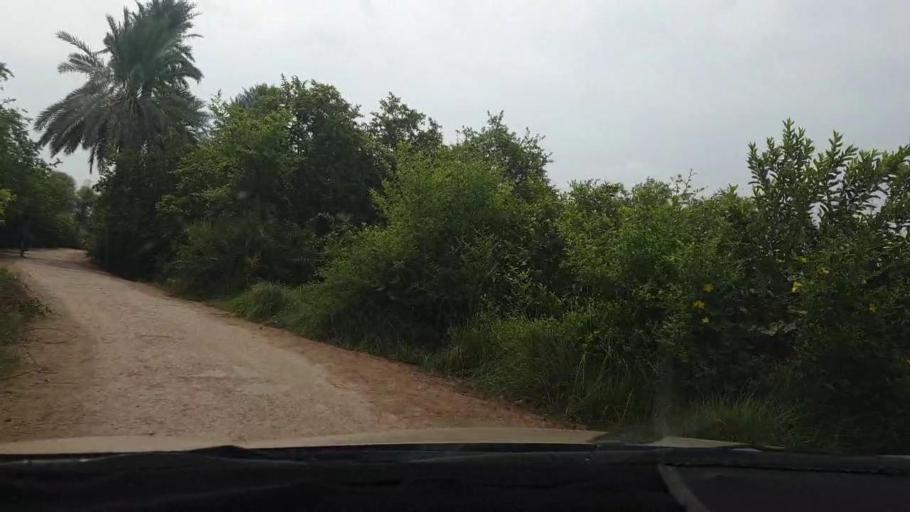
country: PK
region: Sindh
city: Naudero
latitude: 27.6286
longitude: 68.3100
